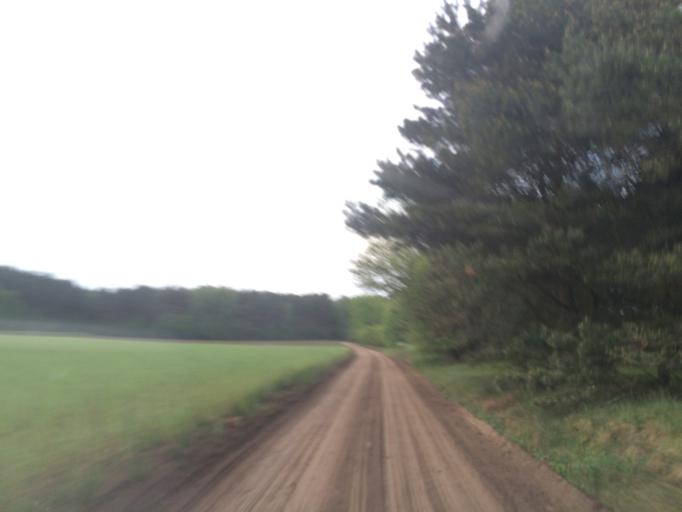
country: PL
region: Warmian-Masurian Voivodeship
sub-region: Powiat nowomiejski
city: Kurzetnik
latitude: 53.3532
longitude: 19.5162
